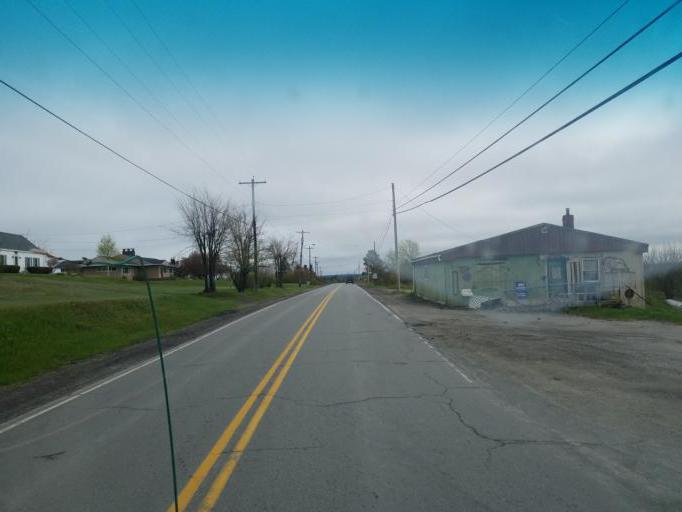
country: US
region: Maine
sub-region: Washington County
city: Eastport
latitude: 44.8428
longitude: -67.0106
